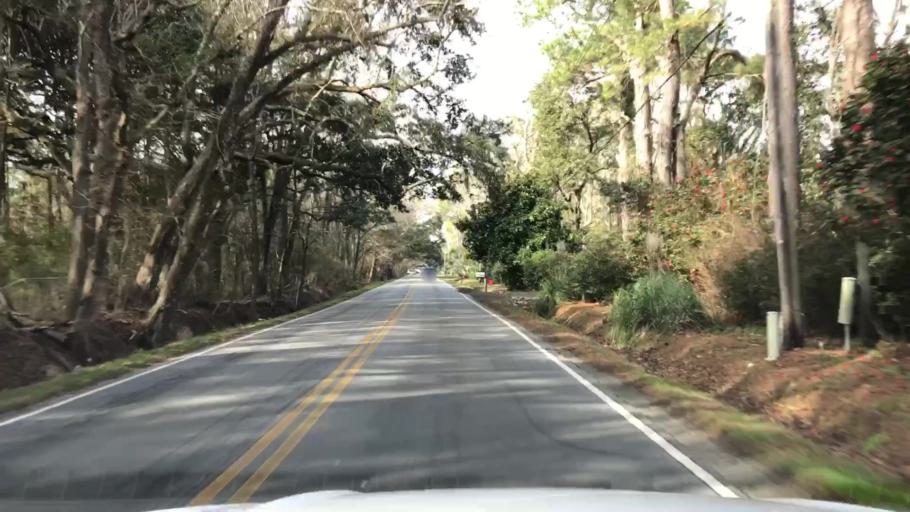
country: US
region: South Carolina
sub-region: Charleston County
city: Shell Point
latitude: 32.7642
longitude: -80.0621
